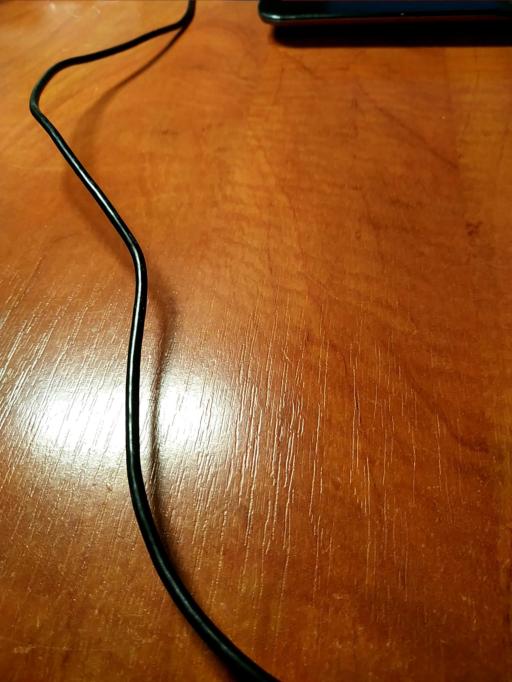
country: BY
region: Mogilev
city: Khotsimsk
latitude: 53.5430
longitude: 32.5053
